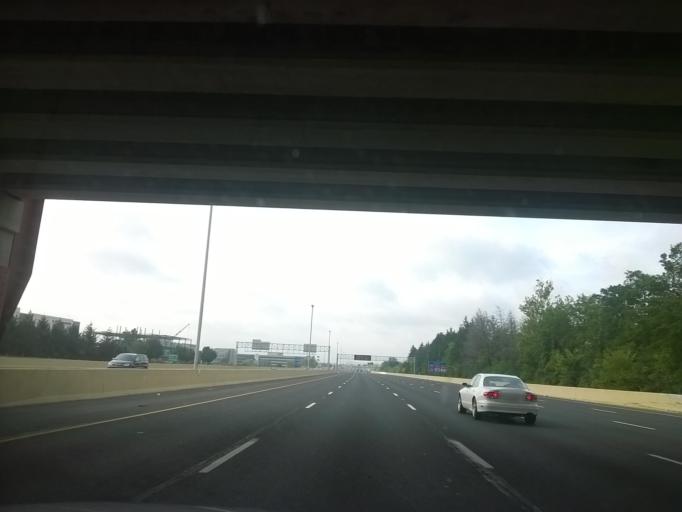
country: US
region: Indiana
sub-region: Boone County
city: Zionsville
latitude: 39.8960
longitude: -86.2698
